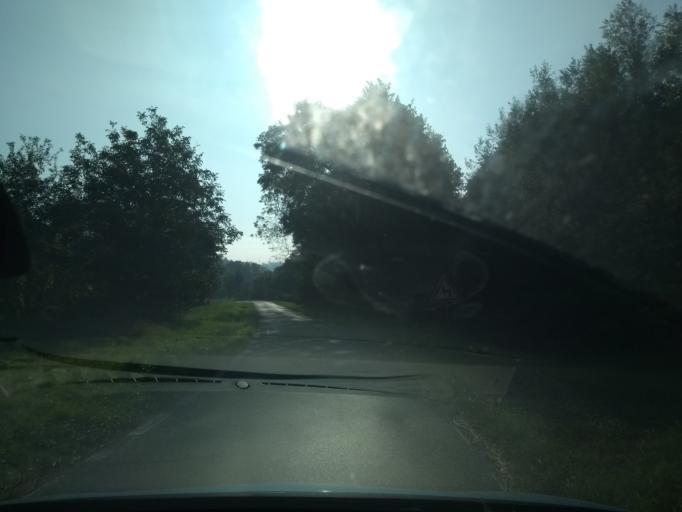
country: IT
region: Piedmont
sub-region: Provincia di Torino
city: Vallo Torinese
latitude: 45.2218
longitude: 7.5029
